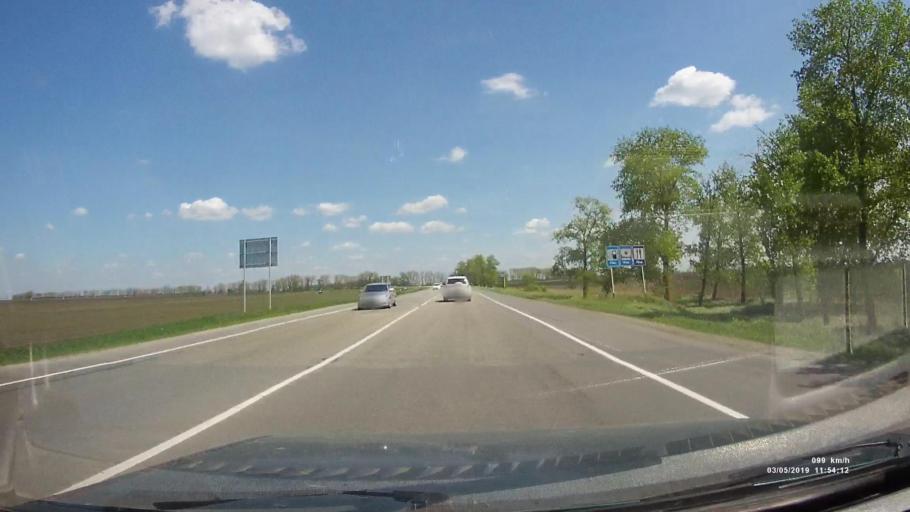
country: RU
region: Rostov
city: Bagayevskaya
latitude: 47.1682
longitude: 40.2754
